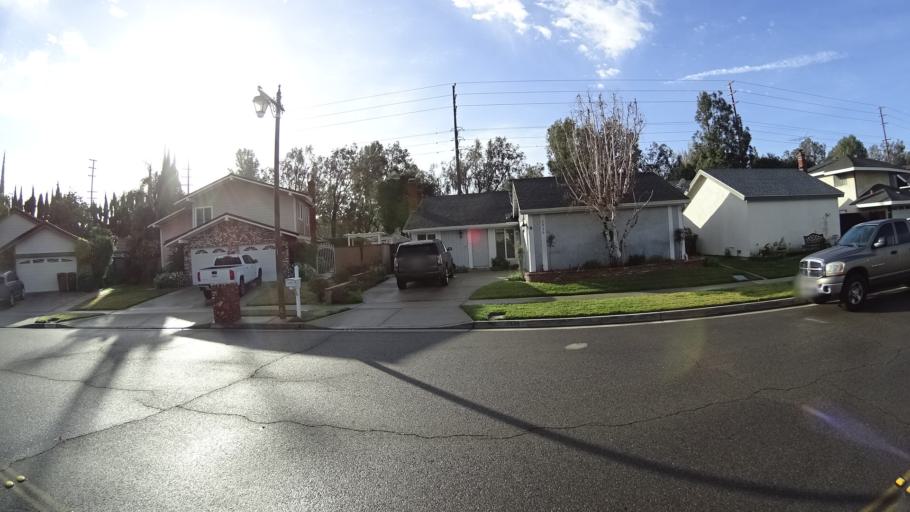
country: US
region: California
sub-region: Orange County
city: Yorba Linda
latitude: 33.8730
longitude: -117.7613
